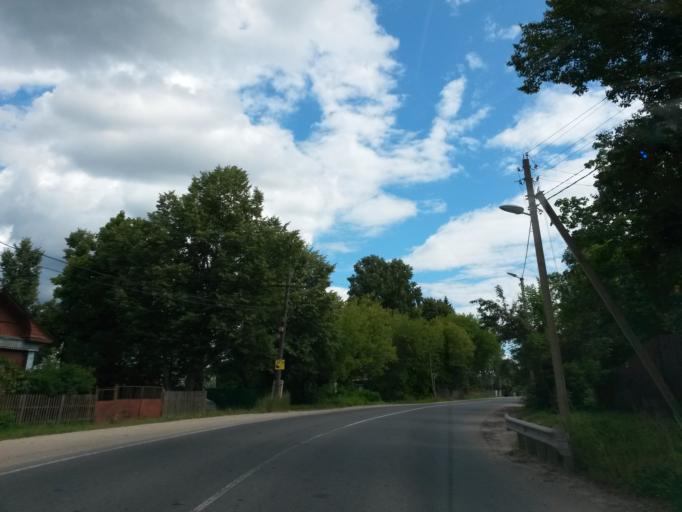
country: RU
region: Ivanovo
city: Novo-Talitsy
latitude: 57.0644
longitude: 40.7095
